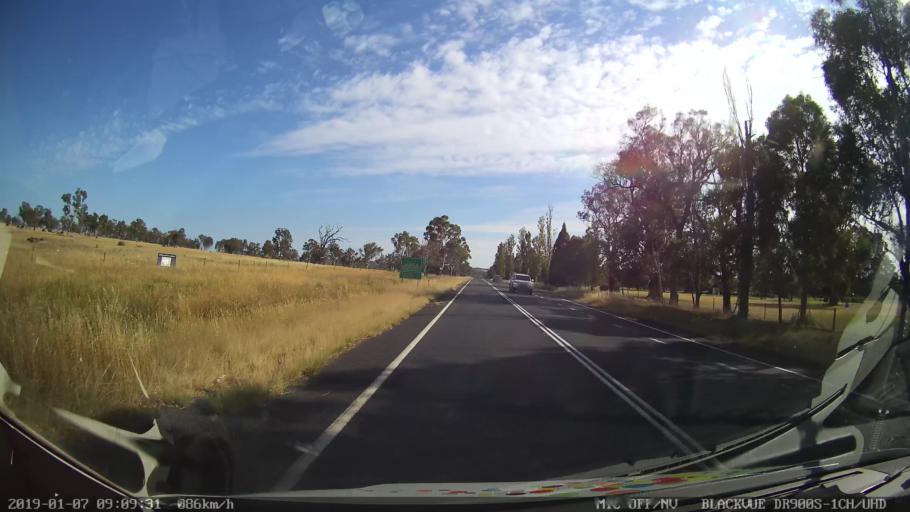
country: AU
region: New South Wales
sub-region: Armidale Dumaresq
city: Armidale
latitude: -30.6567
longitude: 151.4889
